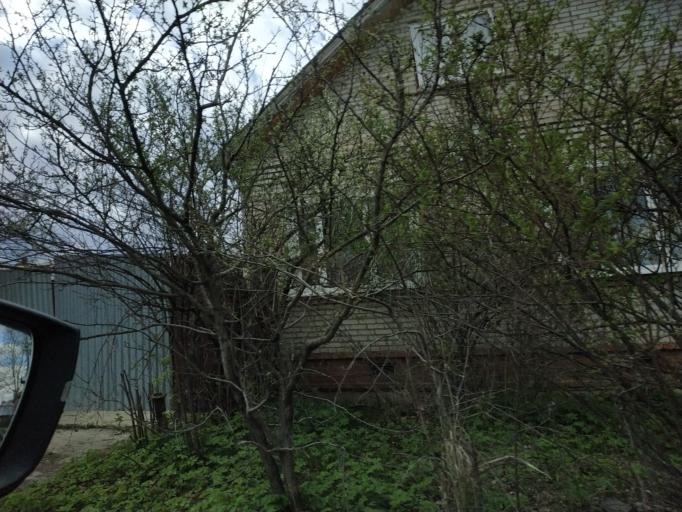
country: RU
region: Moskovskaya
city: Pavlovskiy Posad
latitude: 55.7788
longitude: 38.6400
